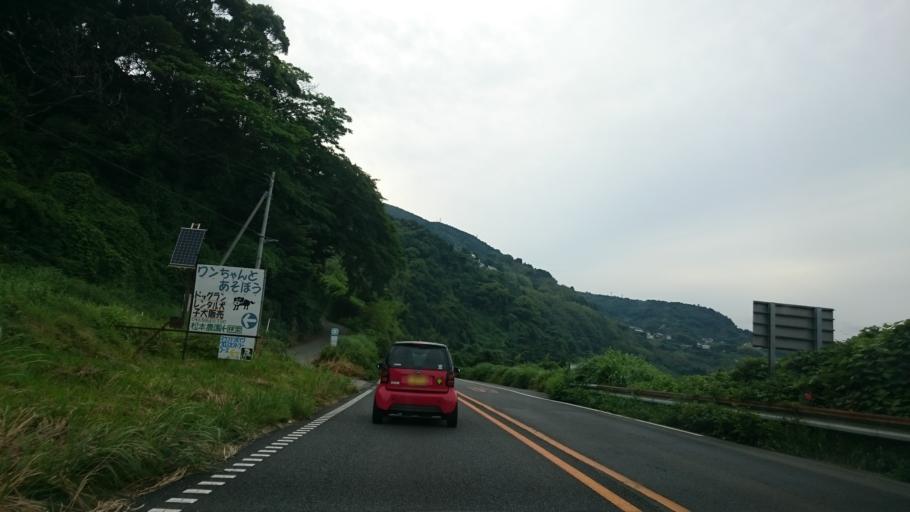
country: JP
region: Kanagawa
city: Yugawara
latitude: 35.1742
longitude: 139.1414
